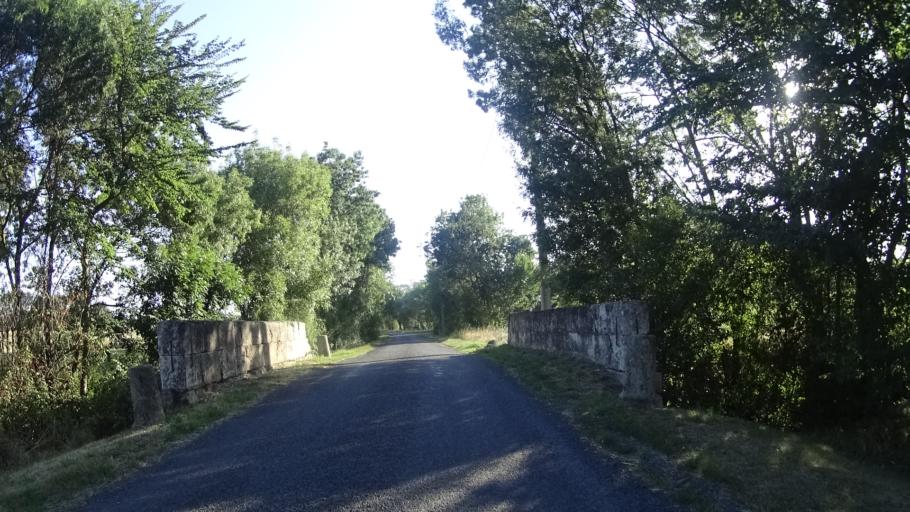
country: FR
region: Pays de la Loire
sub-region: Departement de Maine-et-Loire
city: Villebernier
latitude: 47.2731
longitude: -0.0085
